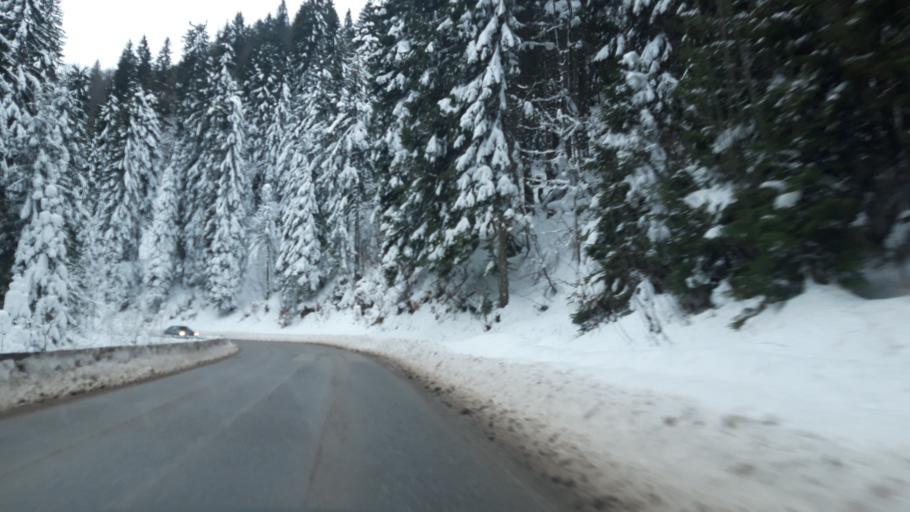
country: BA
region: Republika Srpska
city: Koran
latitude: 43.7455
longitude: 18.5649
